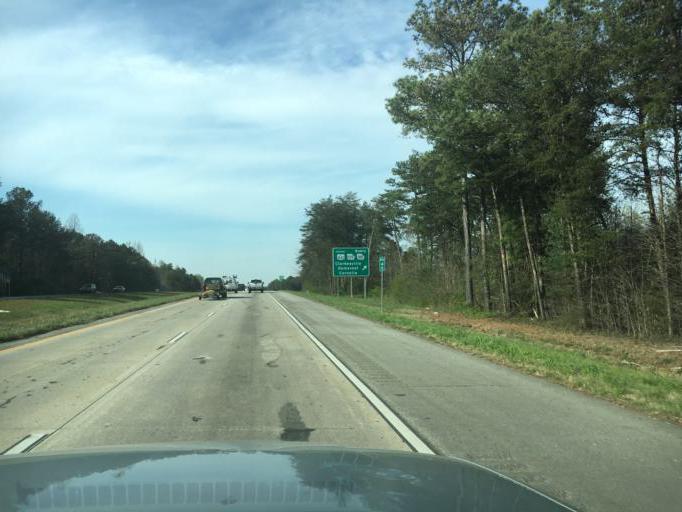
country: US
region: Georgia
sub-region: Habersham County
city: Cornelia
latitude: 34.5304
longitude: -83.5407
